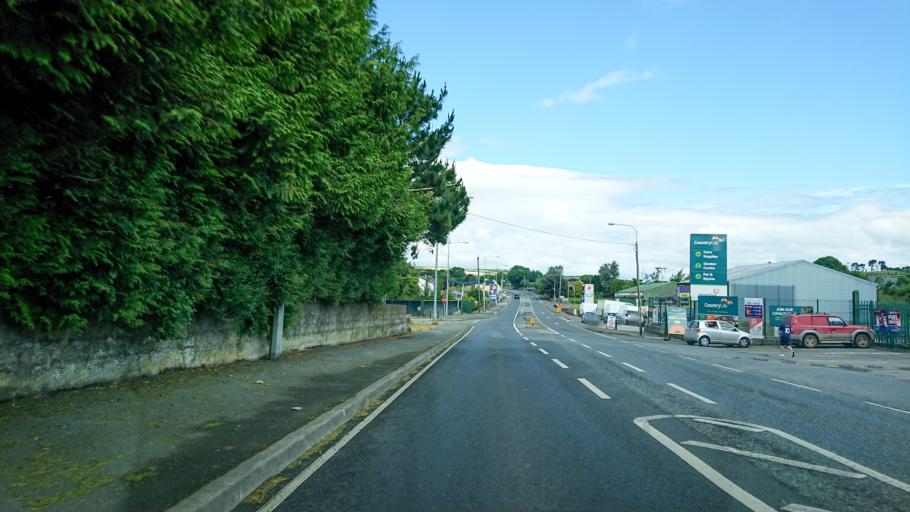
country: IE
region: Leinster
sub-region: Kilkenny
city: Mooncoin
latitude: 52.2328
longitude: -7.2422
